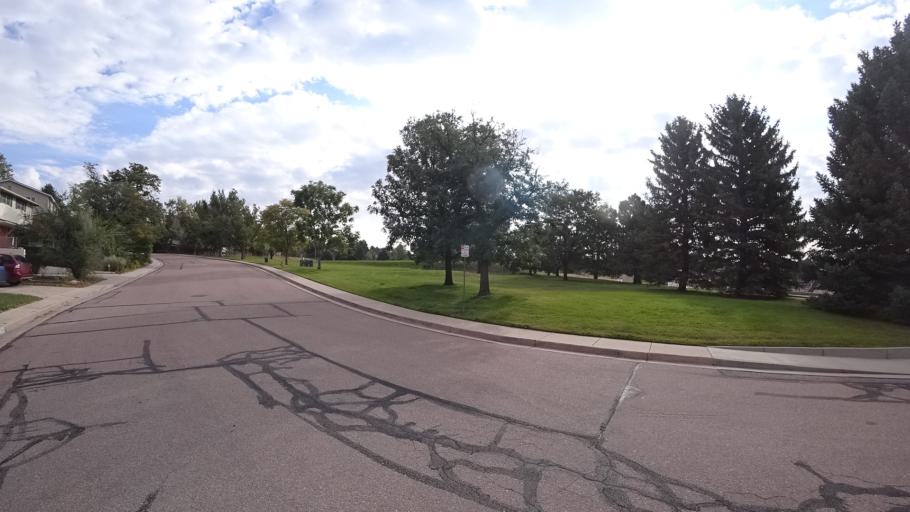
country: US
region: Colorado
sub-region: El Paso County
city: Cimarron Hills
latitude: 38.8633
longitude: -104.7503
